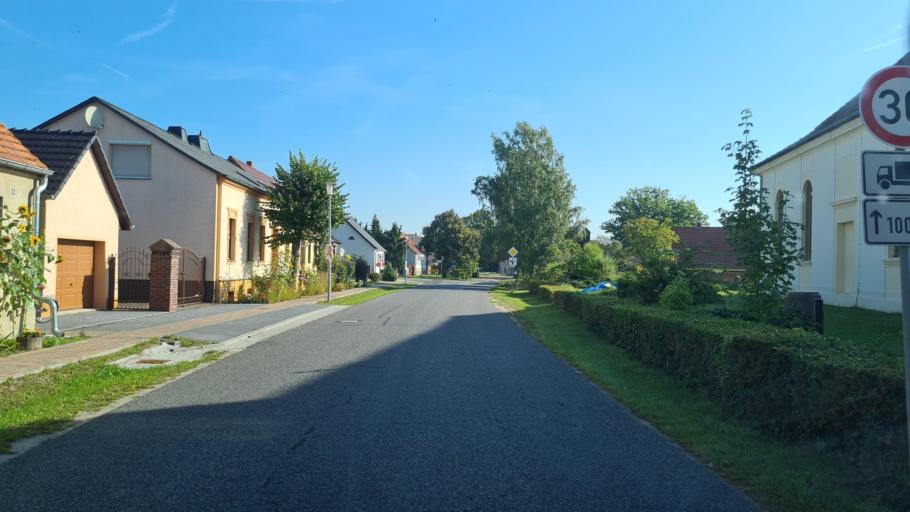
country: DE
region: Brandenburg
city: Pessin
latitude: 52.6719
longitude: 12.6391
